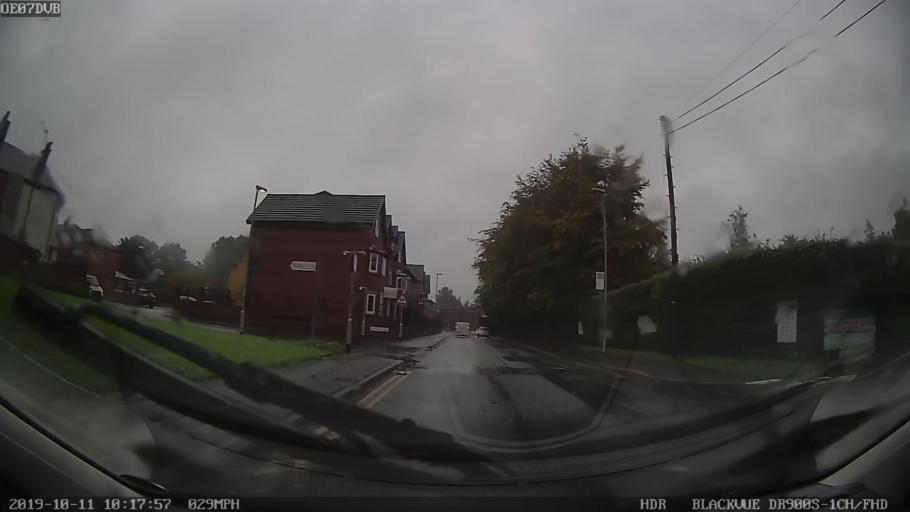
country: GB
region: England
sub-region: Borough of Rochdale
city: Middleton
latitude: 53.5432
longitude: -2.1720
